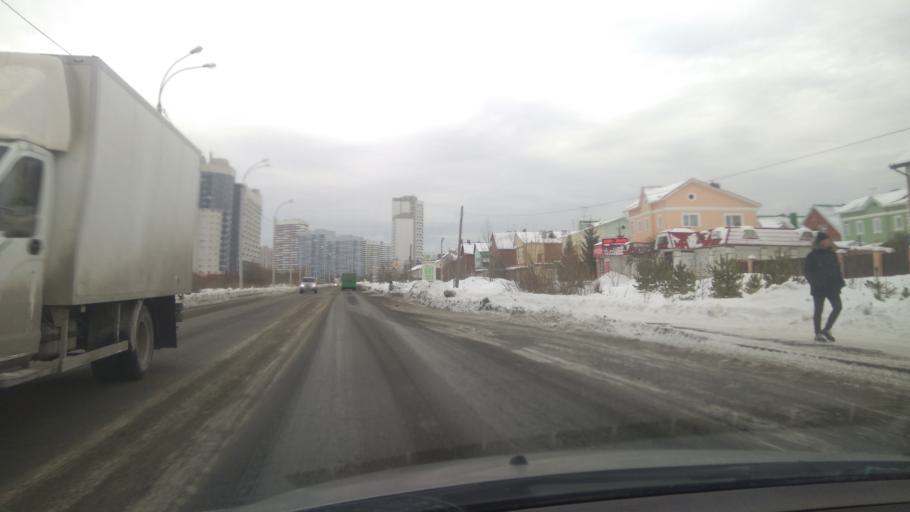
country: RU
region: Sverdlovsk
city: Shirokaya Rechka
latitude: 56.8049
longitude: 60.4947
